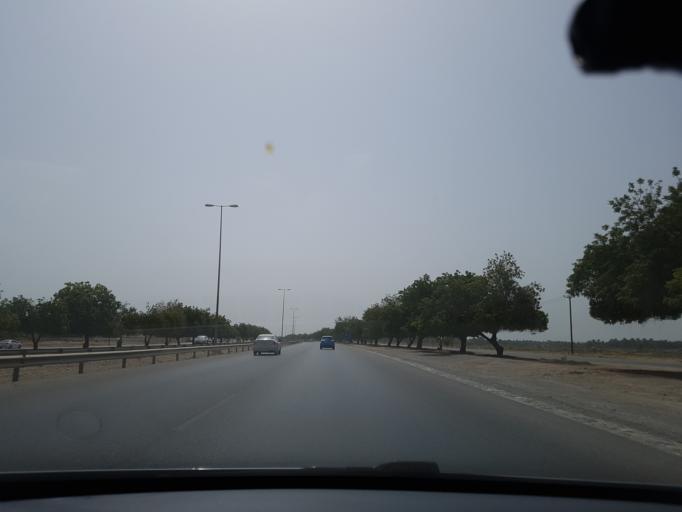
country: OM
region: Al Batinah
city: As Suwayq
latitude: 23.8071
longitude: 57.4685
